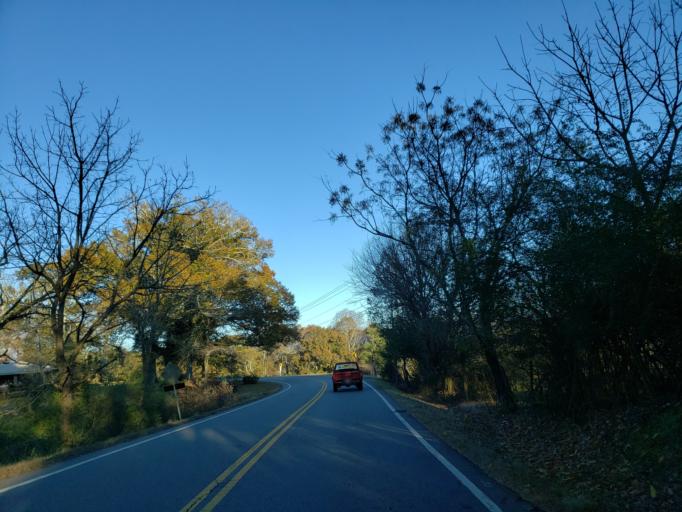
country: US
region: Georgia
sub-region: Cherokee County
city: Canton
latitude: 34.1994
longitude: -84.4185
